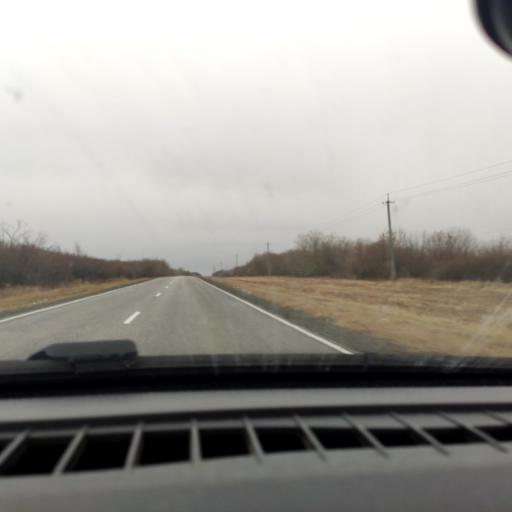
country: RU
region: Voronezj
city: Uryv-Pokrovka
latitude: 51.0949
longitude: 39.0110
